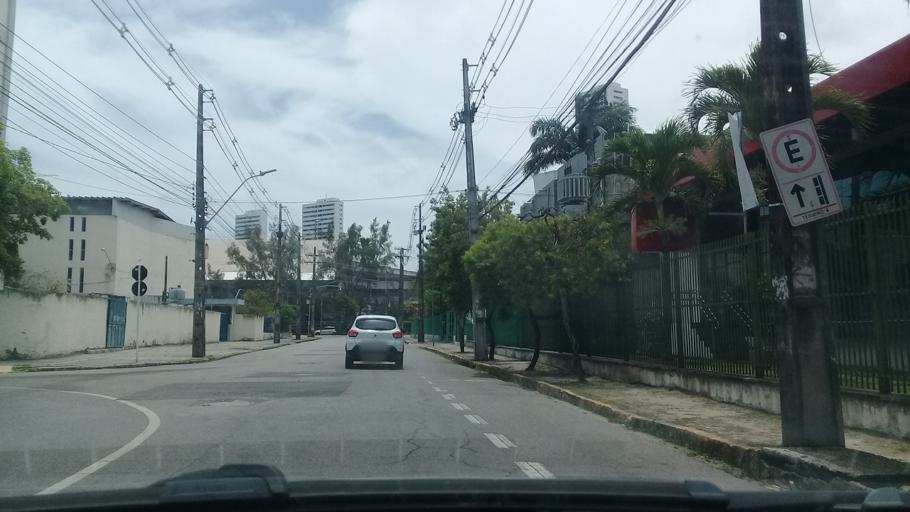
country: BR
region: Pernambuco
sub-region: Recife
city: Recife
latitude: -8.0601
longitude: -34.9038
